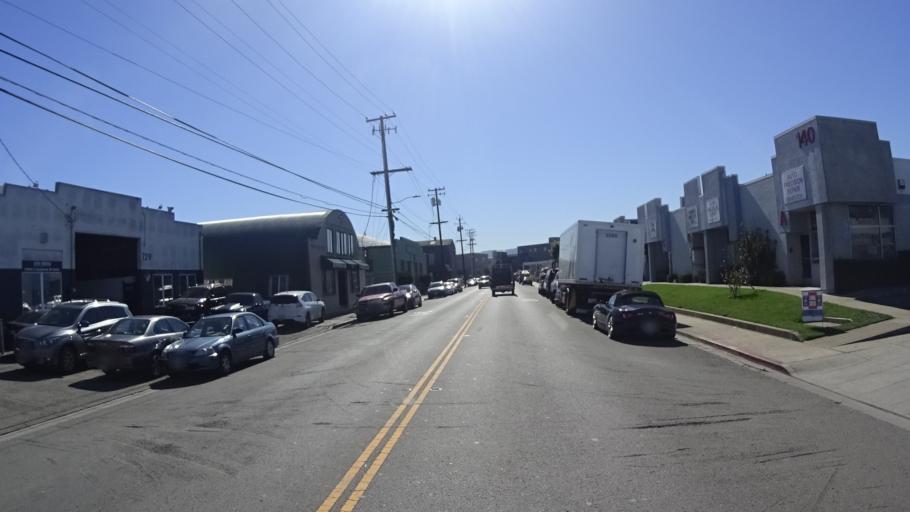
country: US
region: California
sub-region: San Mateo County
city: South San Francisco
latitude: 37.6449
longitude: -122.4137
